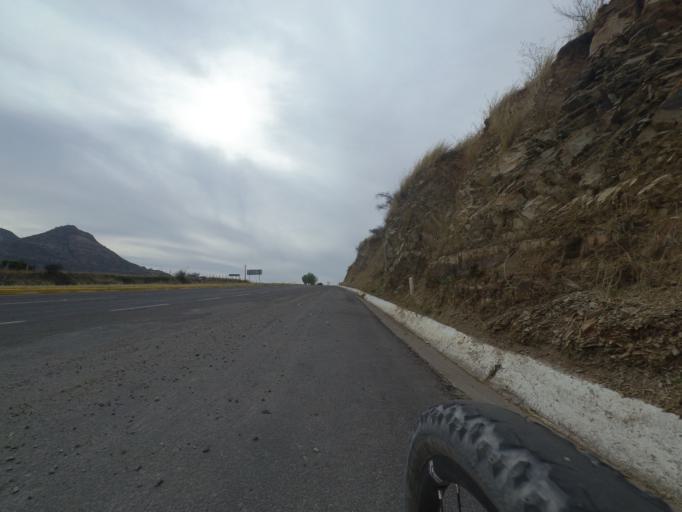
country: MX
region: Aguascalientes
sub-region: Aguascalientes
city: La Loma de los Negritos
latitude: 21.8921
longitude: -102.4019
